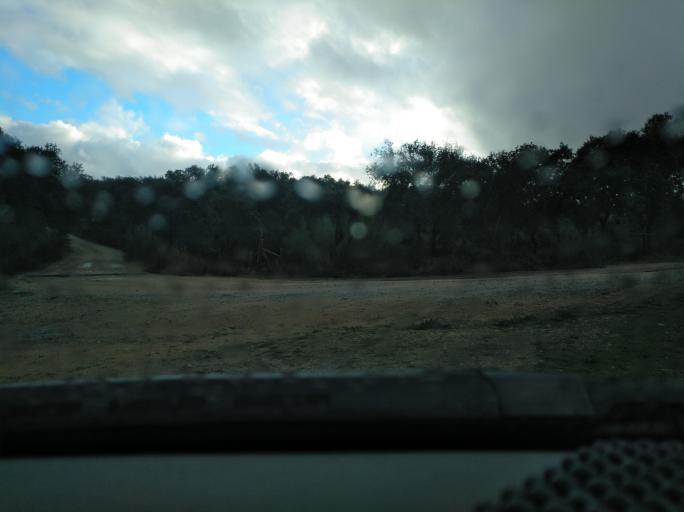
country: PT
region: Portalegre
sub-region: Campo Maior
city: Campo Maior
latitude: 38.9969
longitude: -7.1448
